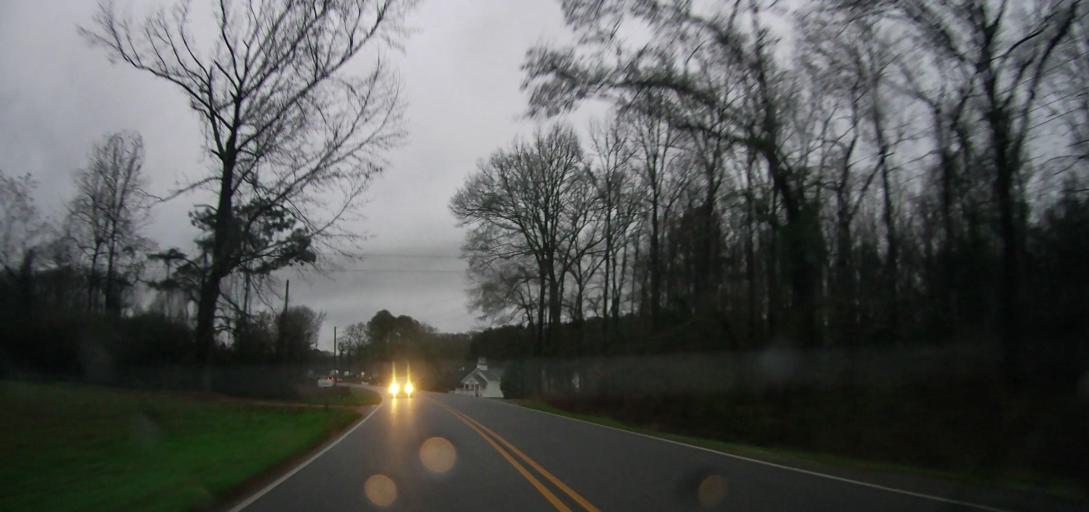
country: US
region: Alabama
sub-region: Tuscaloosa County
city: Vance
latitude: 33.1163
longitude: -87.2211
